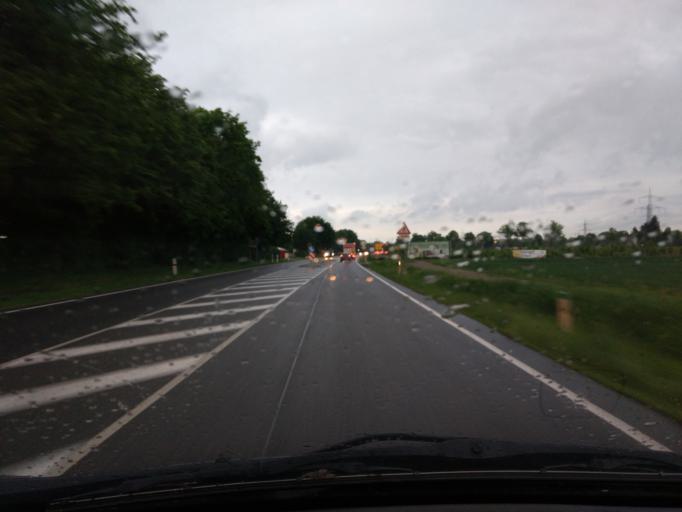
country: DE
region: North Rhine-Westphalia
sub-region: Regierungsbezirk Koln
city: Frechen
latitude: 50.9383
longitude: 6.7960
